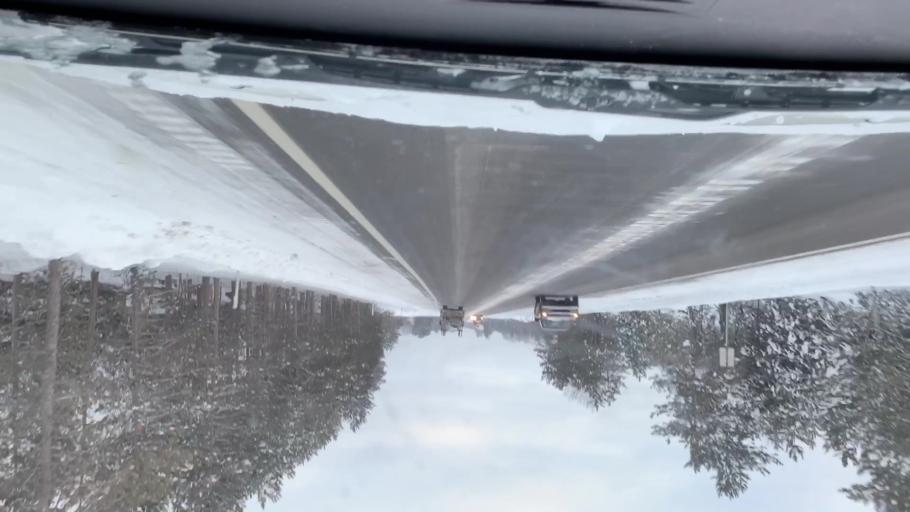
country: US
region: Michigan
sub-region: Kalkaska County
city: Kalkaska
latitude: 44.6823
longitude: -85.2260
